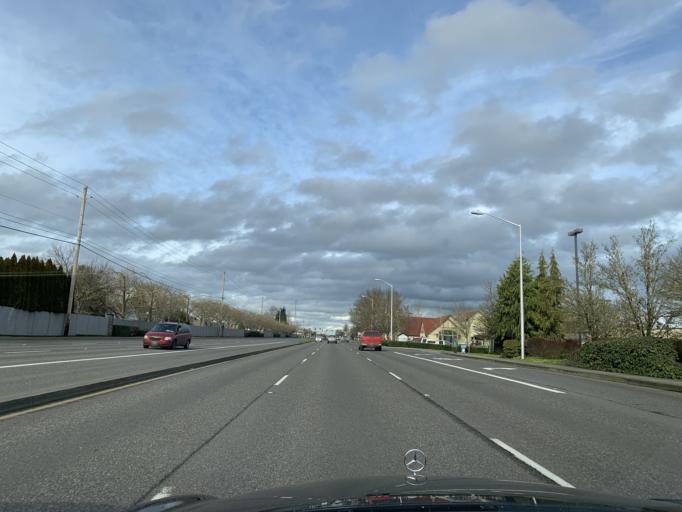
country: US
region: Washington
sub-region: Clark County
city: Mill Plain
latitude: 45.6069
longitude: -122.5039
